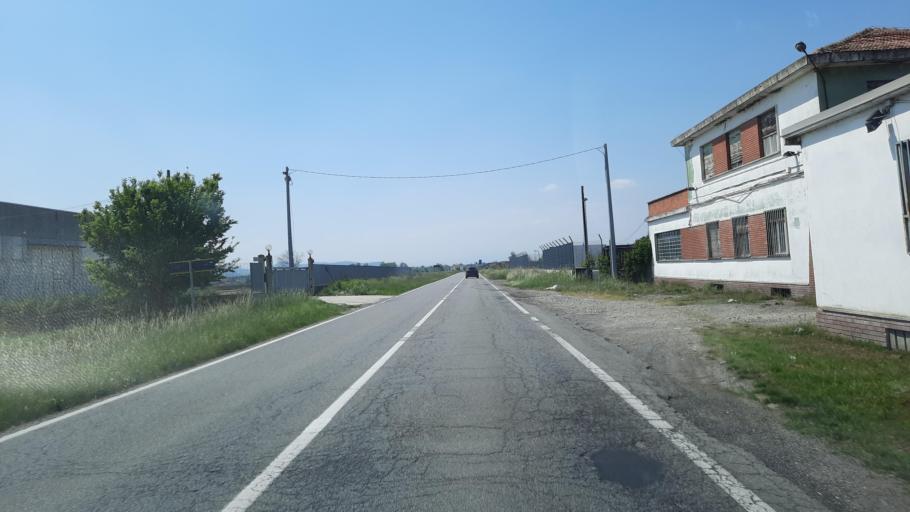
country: IT
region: Piedmont
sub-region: Provincia di Vercelli
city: Crescentino
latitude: 45.1936
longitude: 8.0785
